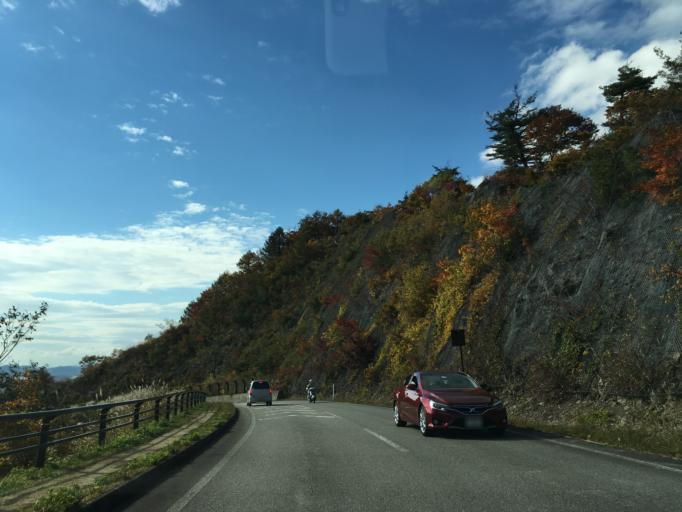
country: JP
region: Fukushima
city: Inawashiro
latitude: 37.6763
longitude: 140.1245
